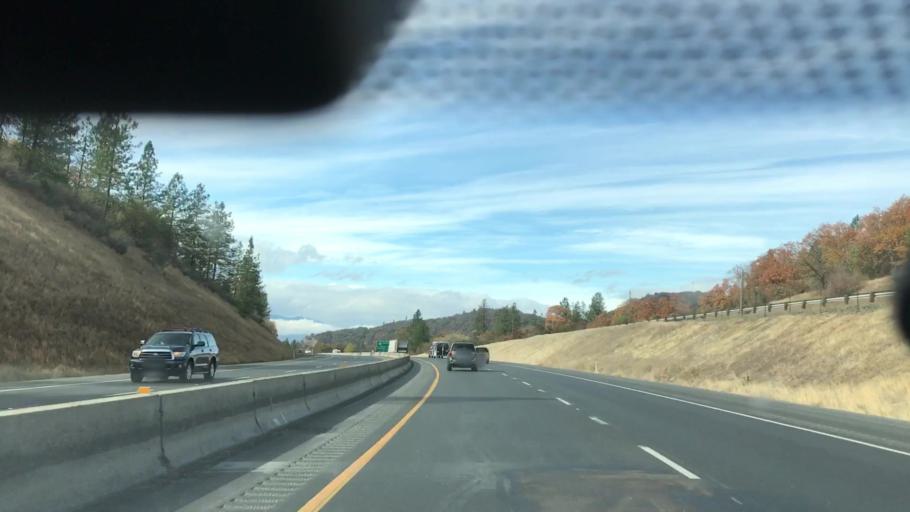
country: US
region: Oregon
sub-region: Josephine County
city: Fruitdale
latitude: 42.4368
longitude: -123.2650
